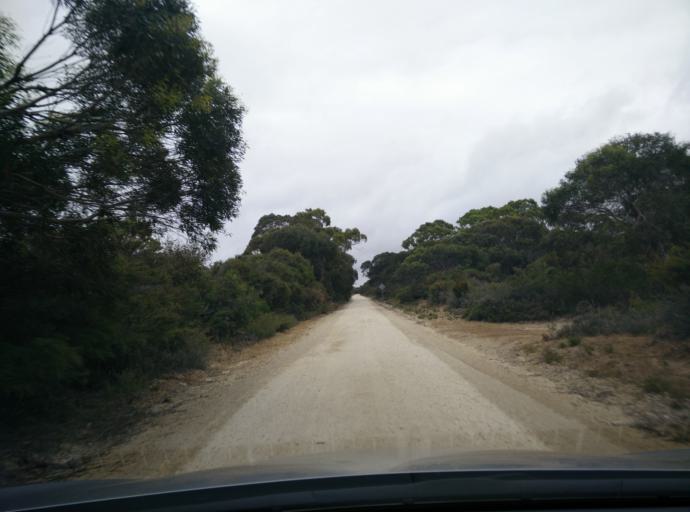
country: AU
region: South Australia
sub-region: Kangaroo Island
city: Kingscote
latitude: -35.8738
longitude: 137.5018
